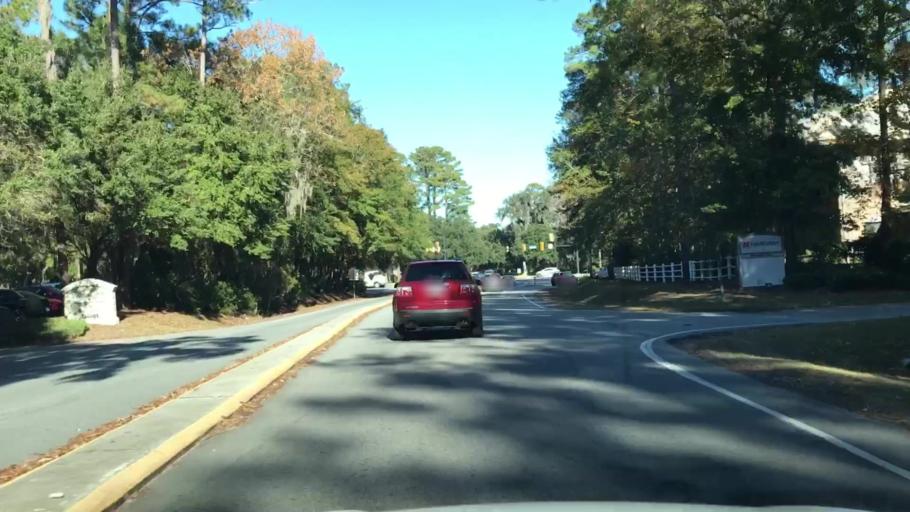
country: US
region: South Carolina
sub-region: Beaufort County
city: Bluffton
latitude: 32.2773
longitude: -80.8734
